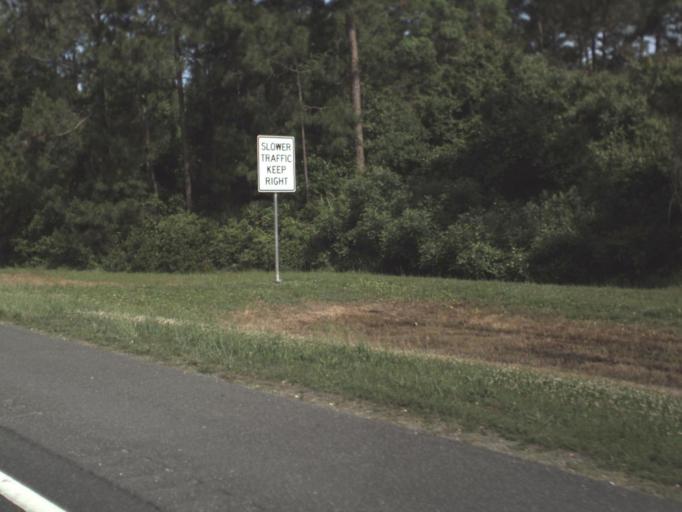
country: US
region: Florida
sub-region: Saint Johns County
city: Ponte Vedra Beach
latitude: 30.2514
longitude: -81.4806
